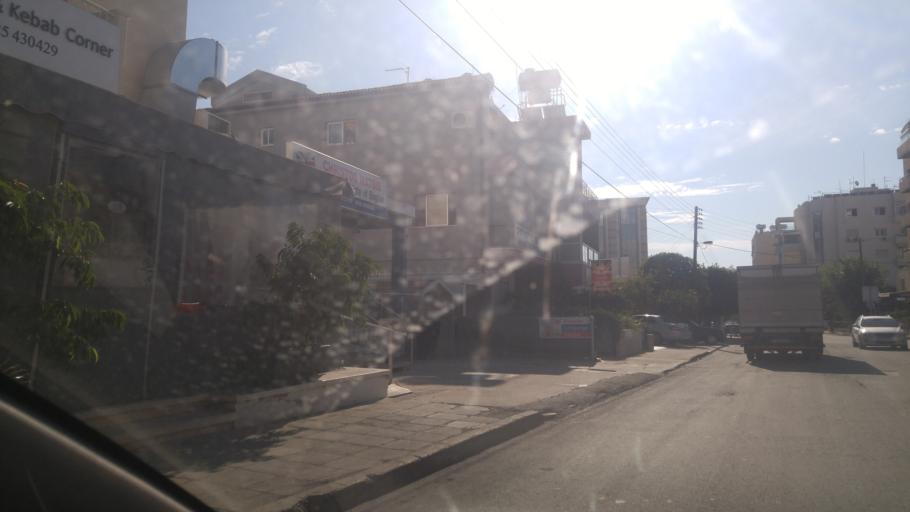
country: CY
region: Limassol
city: Limassol
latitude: 34.6944
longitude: 33.0512
